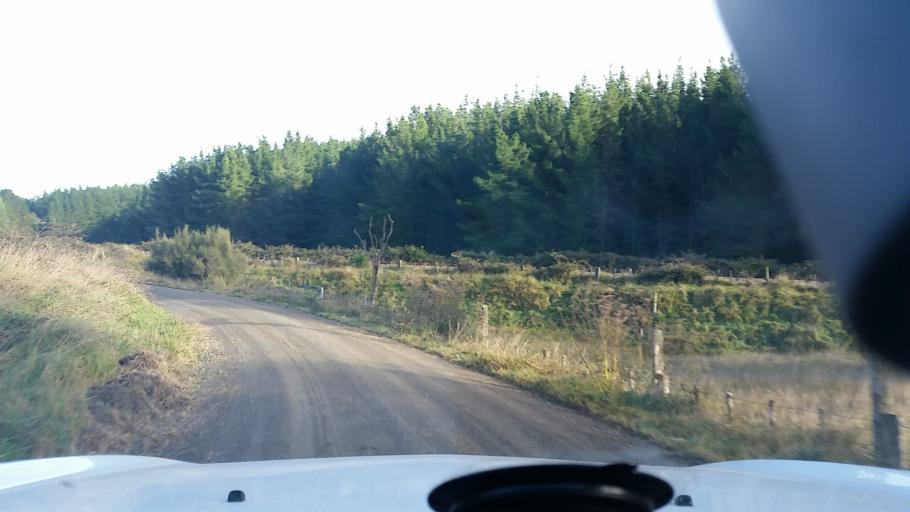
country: NZ
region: Hawke's Bay
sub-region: Napier City
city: Napier
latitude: -39.2409
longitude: 176.8111
